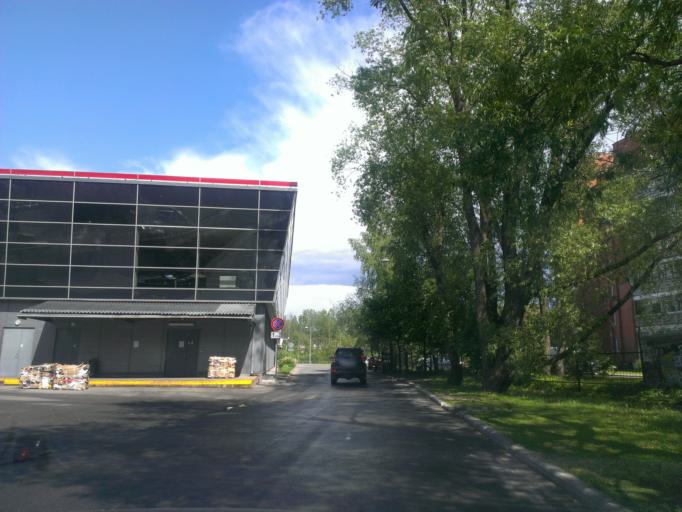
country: LV
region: Riga
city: Bergi
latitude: 56.9890
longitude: 24.2446
